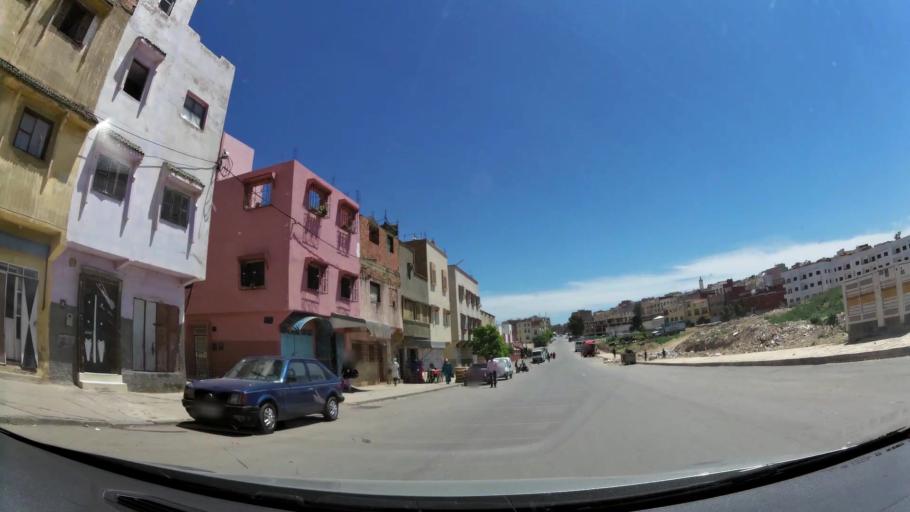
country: MA
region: Meknes-Tafilalet
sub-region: Meknes
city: Meknes
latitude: 33.9065
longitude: -5.5802
